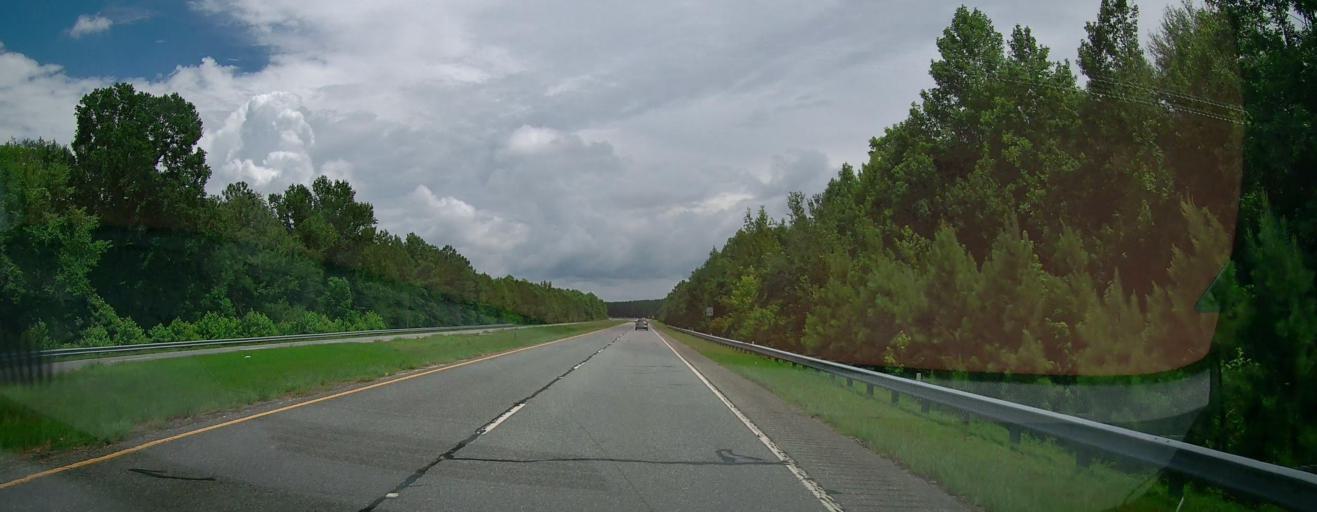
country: US
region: Georgia
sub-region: Dodge County
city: Eastman
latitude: 32.1849
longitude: -83.1986
